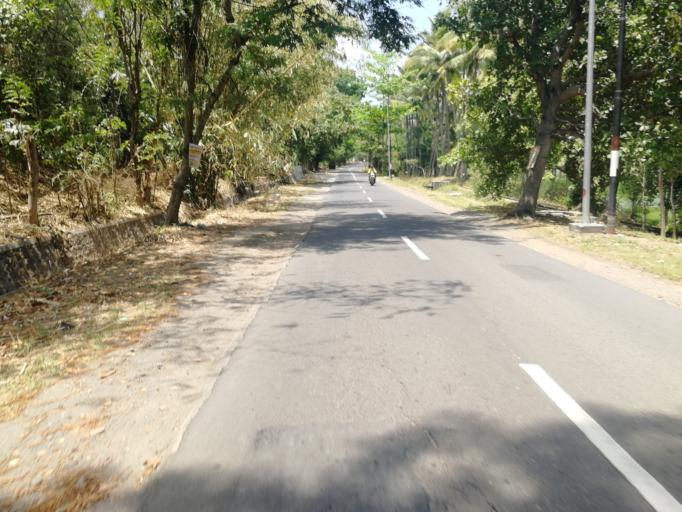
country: ID
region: West Nusa Tenggara
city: Karangsubagan
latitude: -8.4194
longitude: 116.0955
